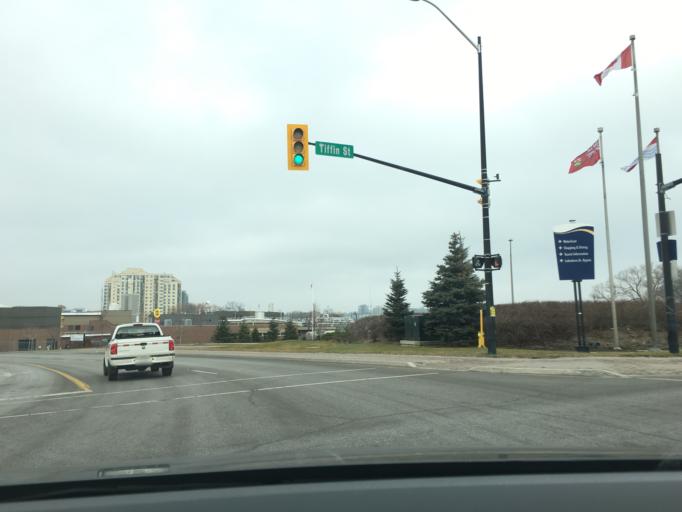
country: CA
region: Ontario
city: Barrie
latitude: 44.3746
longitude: -79.6904
